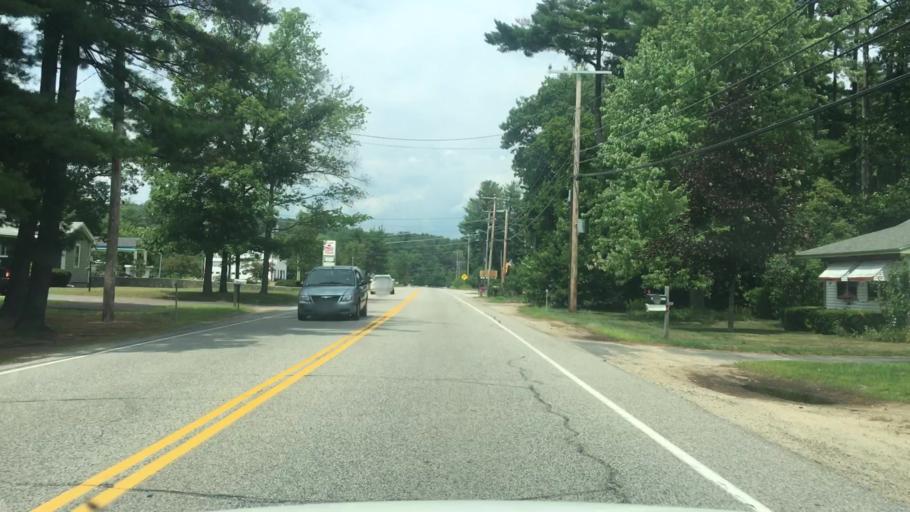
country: US
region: New Hampshire
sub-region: Strafford County
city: Rochester
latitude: 43.3525
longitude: -70.9774
